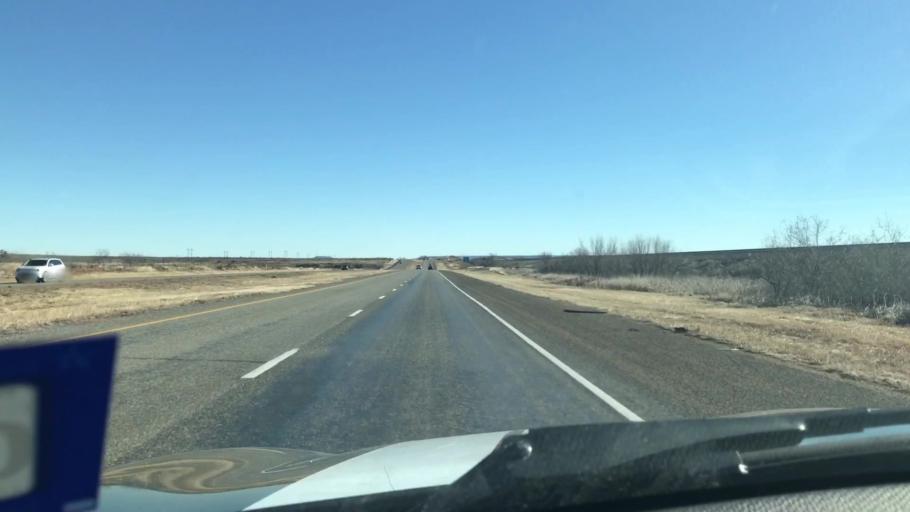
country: US
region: Texas
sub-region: Garza County
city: Post
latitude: 33.1155
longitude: -101.2760
